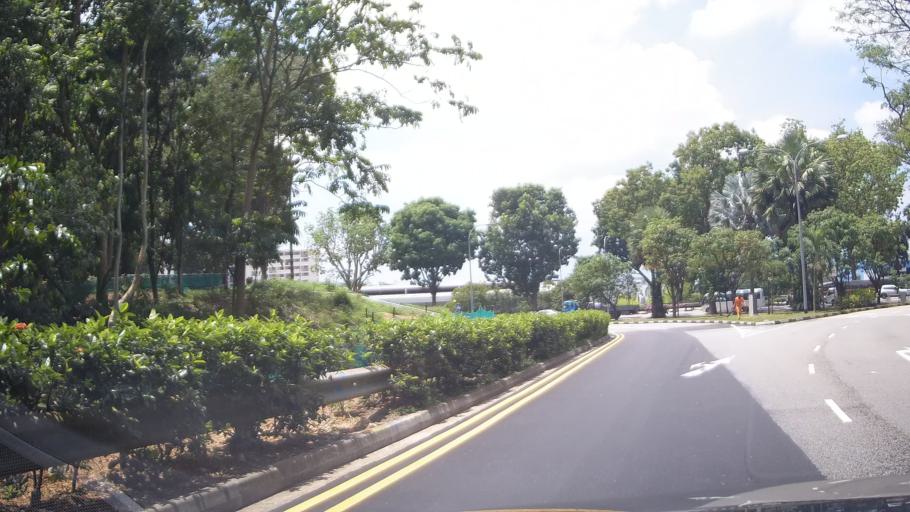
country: MY
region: Johor
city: Johor Bahru
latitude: 1.3316
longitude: 103.6758
